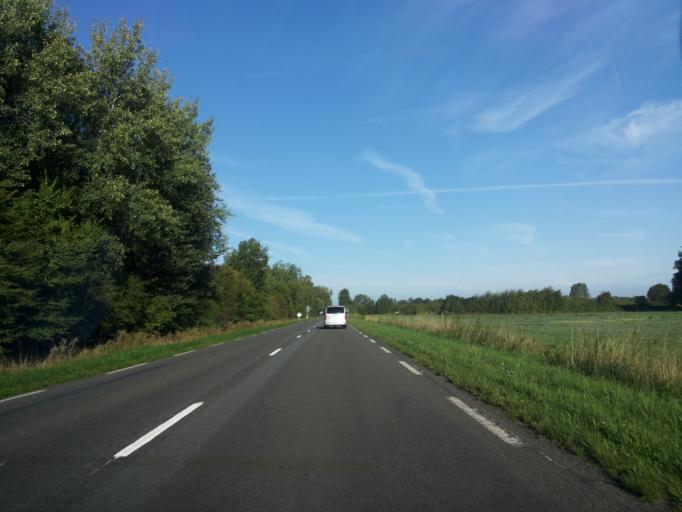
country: FR
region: Picardie
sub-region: Departement de l'Aisne
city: Athies-sous-Laon
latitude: 49.5414
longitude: 3.7388
